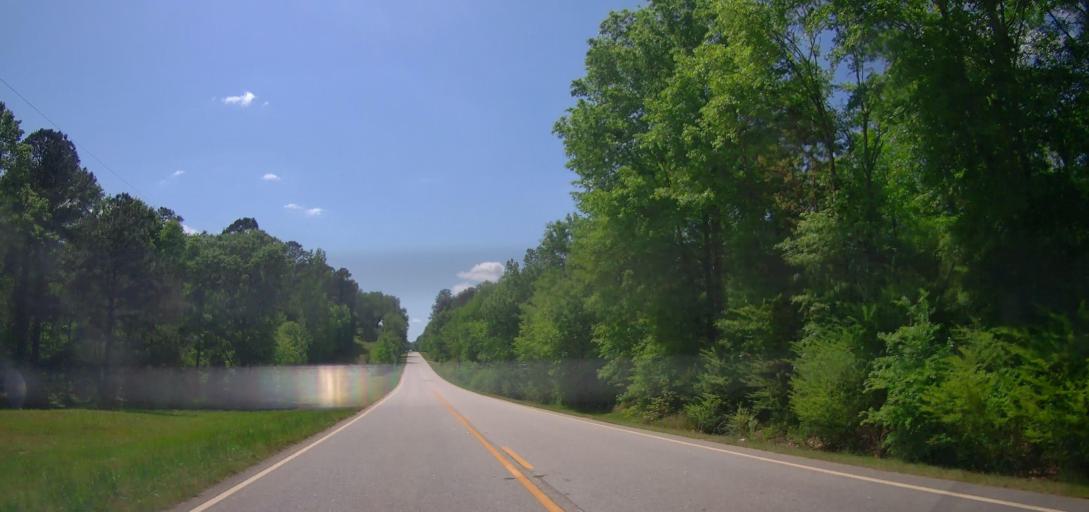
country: US
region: Georgia
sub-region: Putnam County
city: Eatonton
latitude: 33.3404
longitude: -83.3425
